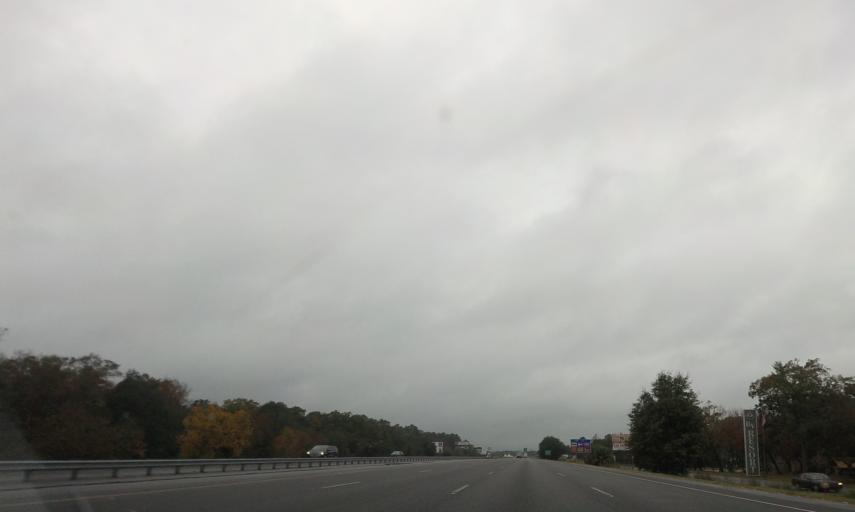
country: US
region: Georgia
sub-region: Lowndes County
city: Valdosta
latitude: 30.6686
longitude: -83.2124
